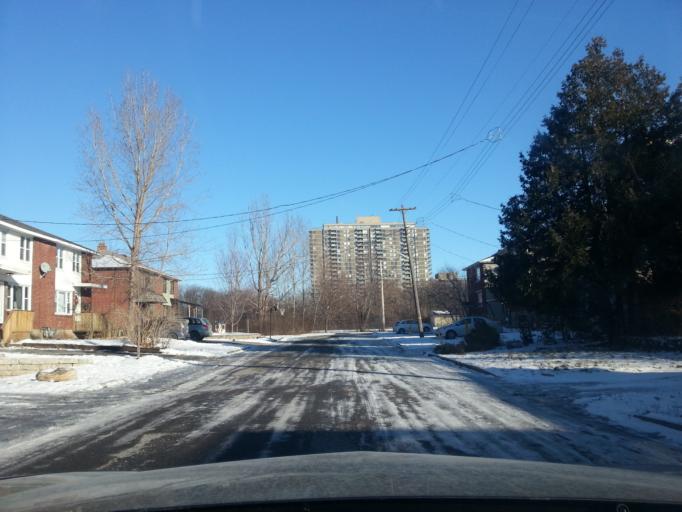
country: CA
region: Ontario
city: Ottawa
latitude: 45.3997
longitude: -75.7566
